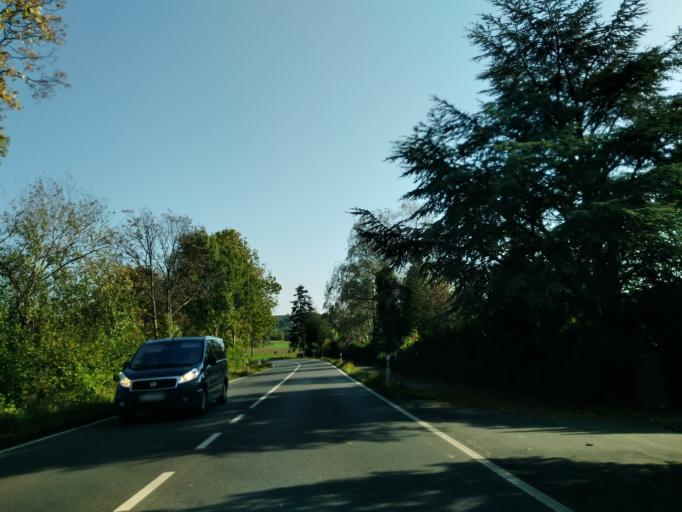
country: DE
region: Rheinland-Pfalz
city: Asbach
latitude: 50.7236
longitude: 7.3754
